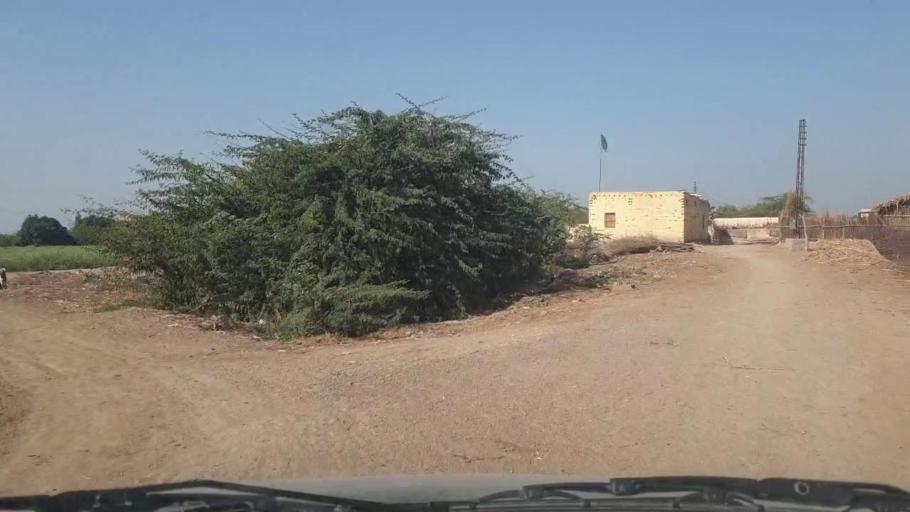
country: PK
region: Sindh
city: Samaro
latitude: 25.2997
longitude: 69.2902
